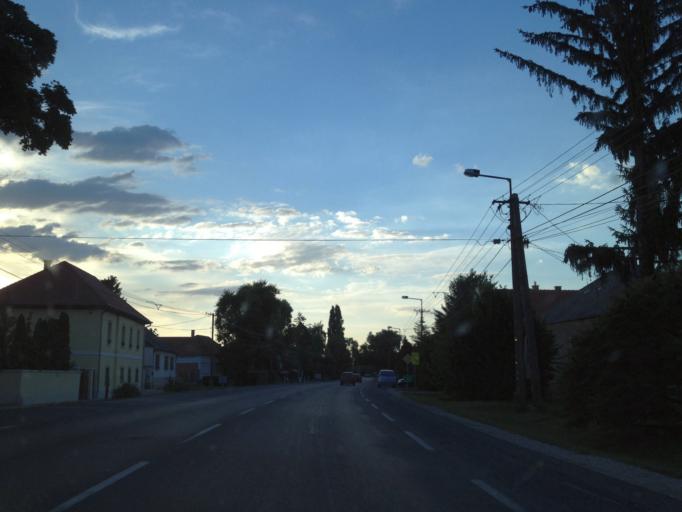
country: HU
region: Gyor-Moson-Sopron
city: Otteveny
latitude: 47.7250
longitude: 17.4910
